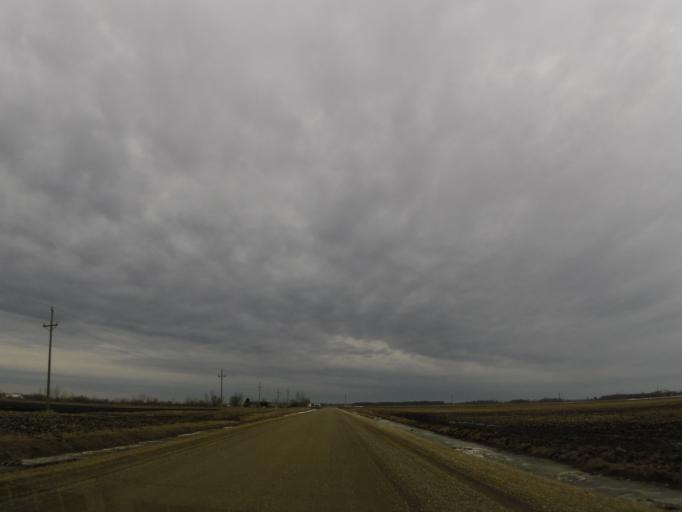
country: US
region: North Dakota
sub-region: Walsh County
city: Grafton
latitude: 48.4198
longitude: -97.4432
